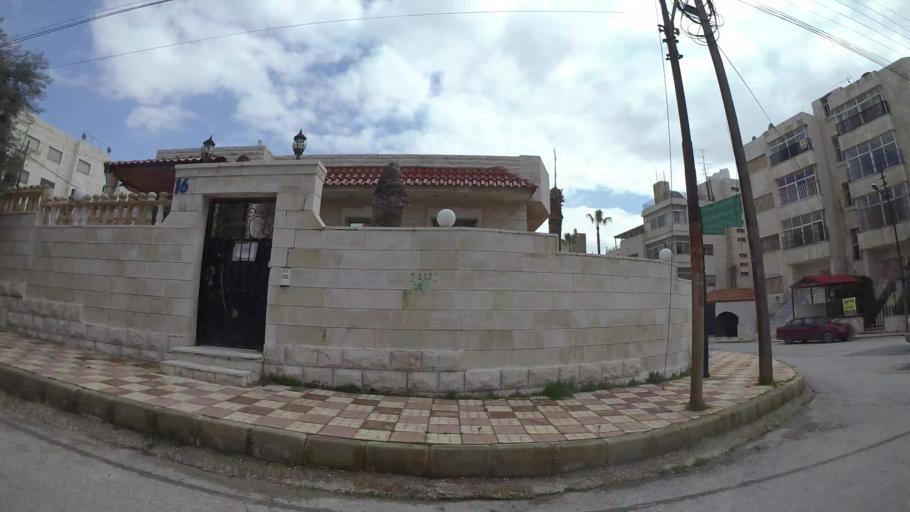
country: JO
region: Amman
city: Amman
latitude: 31.9808
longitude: 35.8971
